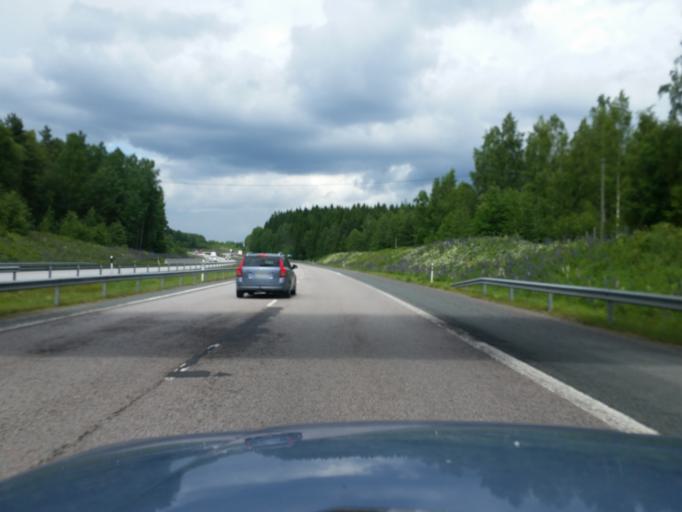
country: FI
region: Paijanne Tavastia
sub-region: Lahti
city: Nastola
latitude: 61.0180
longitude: 25.8279
